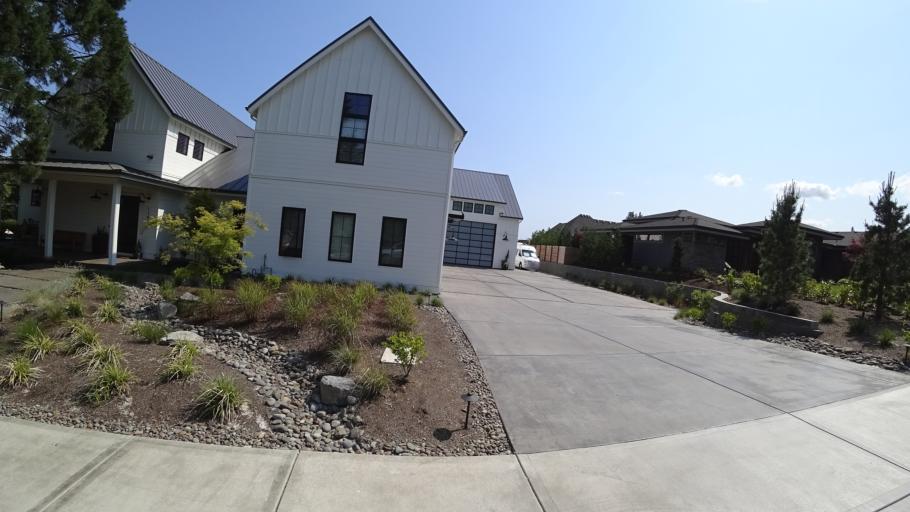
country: US
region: Oregon
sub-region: Clackamas County
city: Happy Valley
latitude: 45.4461
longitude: -122.5318
